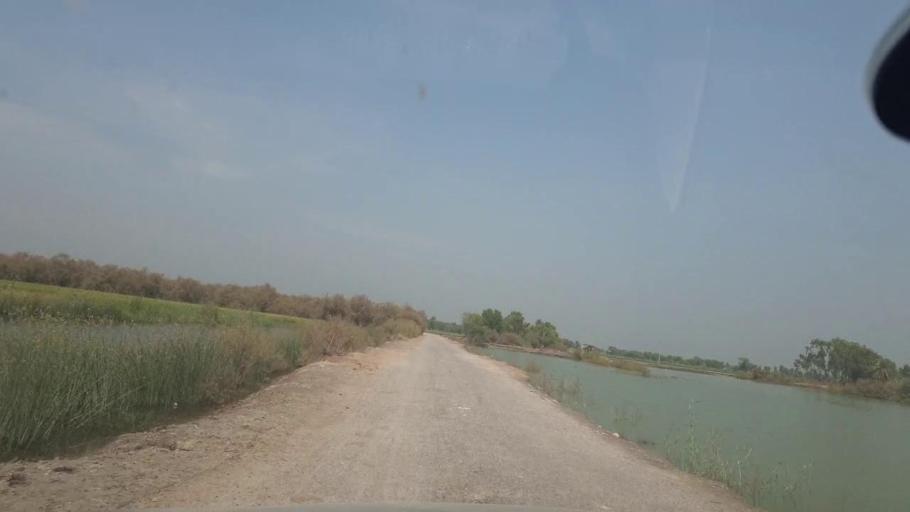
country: PK
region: Sindh
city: Thul
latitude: 28.1691
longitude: 68.6349
